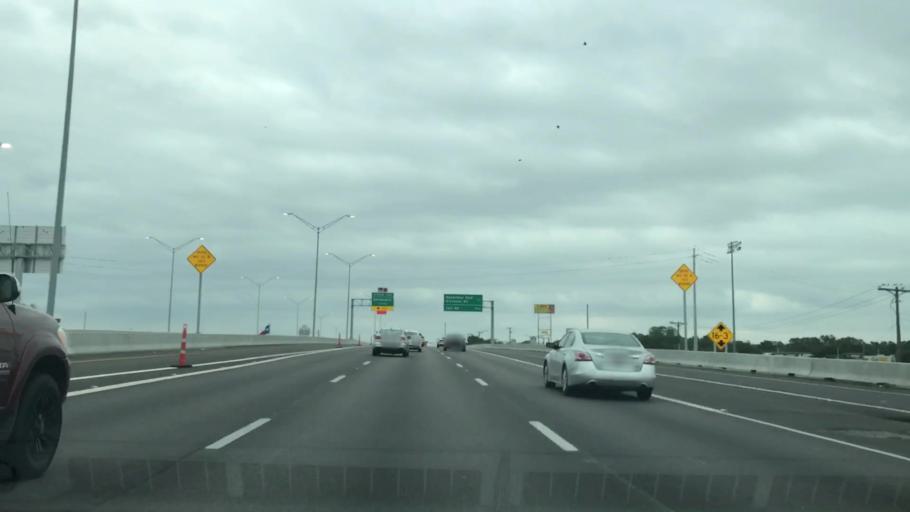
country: US
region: Texas
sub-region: Dallas County
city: Irving
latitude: 32.8370
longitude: -96.9786
